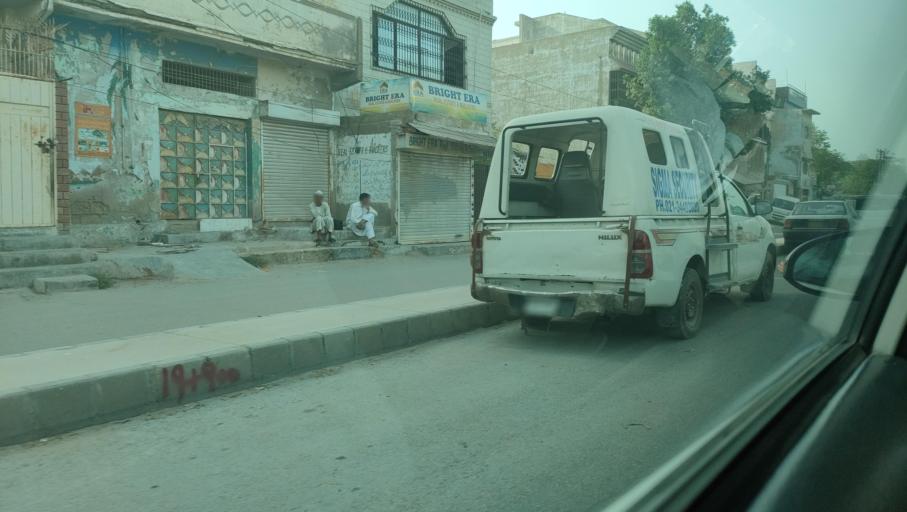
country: PK
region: Sindh
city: Malir Cantonment
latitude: 24.9078
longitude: 67.1835
